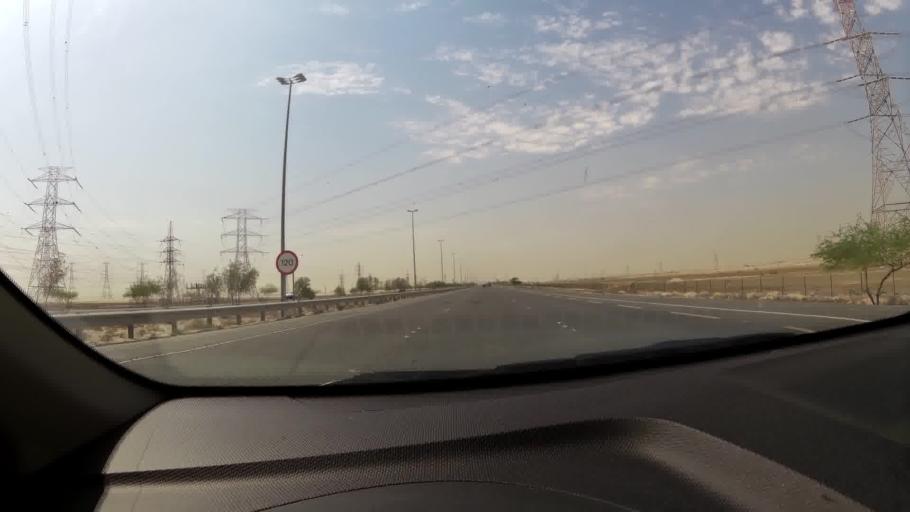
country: KW
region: Al Ahmadi
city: Al Fahahil
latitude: 28.7548
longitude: 48.2808
